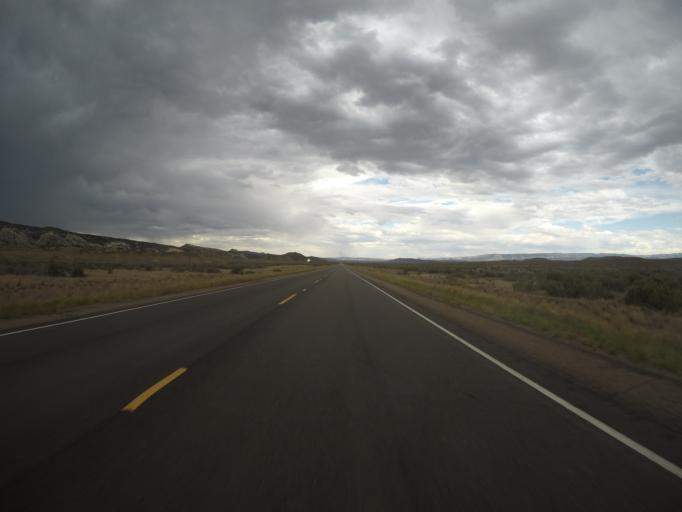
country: US
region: Colorado
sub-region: Rio Blanco County
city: Rangely
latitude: 40.2505
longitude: -108.7771
